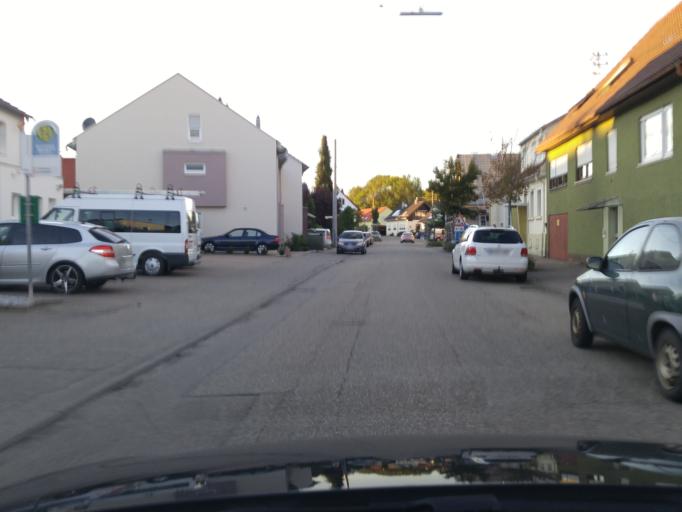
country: DE
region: Baden-Wuerttemberg
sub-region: Regierungsbezirk Stuttgart
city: Bad Wimpfen
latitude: 49.1966
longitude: 9.1387
